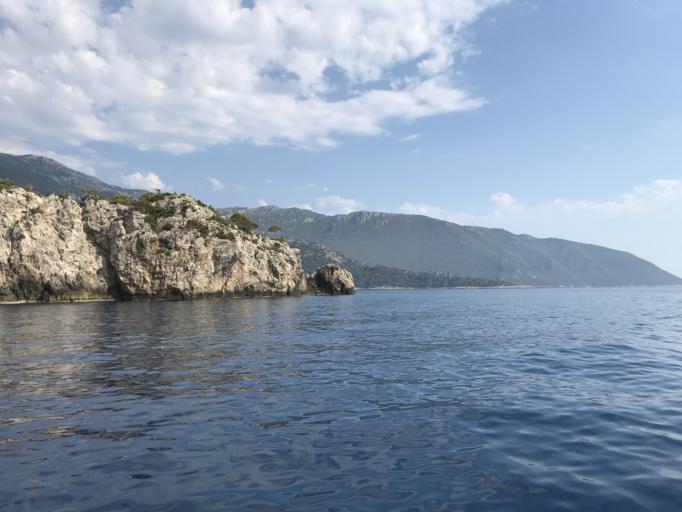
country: TR
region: Mugla
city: OEluedeniz
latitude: 36.4439
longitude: 29.1209
